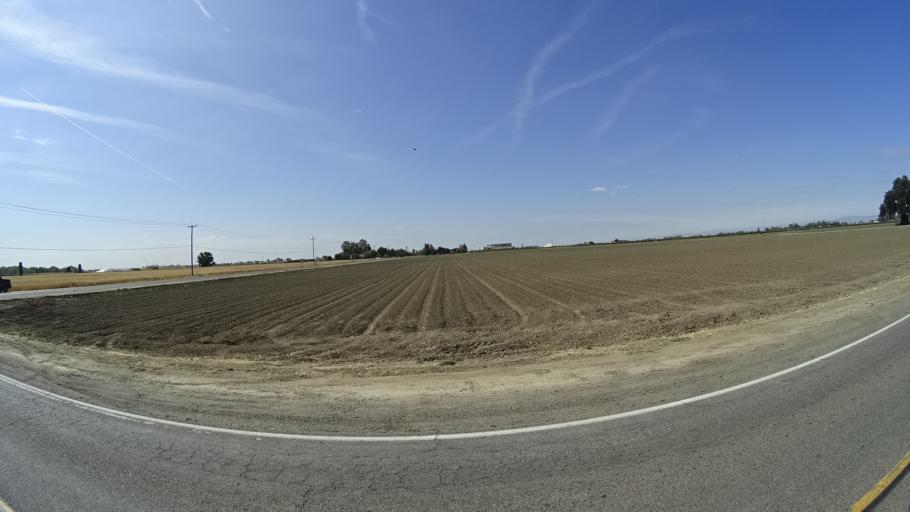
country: US
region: California
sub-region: Kings County
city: Lemoore
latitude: 36.2547
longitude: -119.7633
